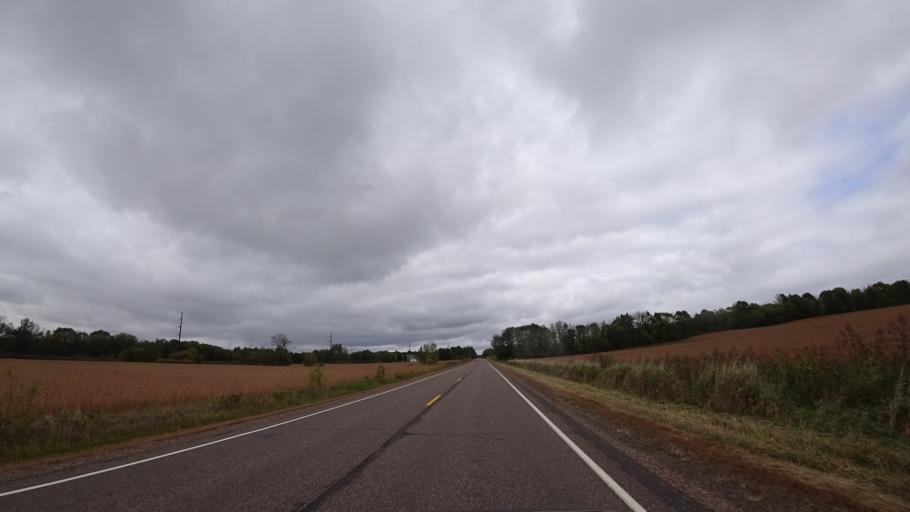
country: US
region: Wisconsin
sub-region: Chippewa County
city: Lake Wissota
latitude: 45.0149
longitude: -91.2867
